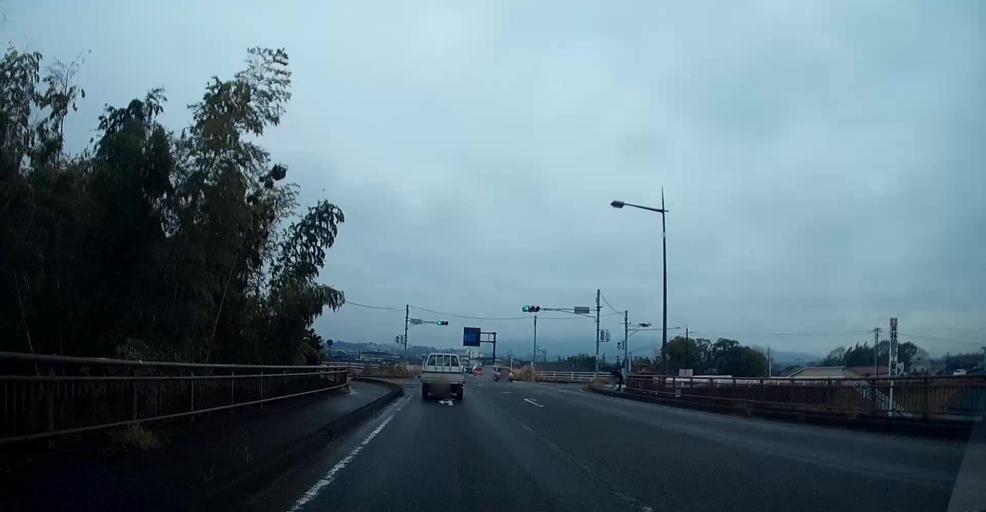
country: JP
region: Kumamoto
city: Kumamoto
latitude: 32.7338
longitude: 130.7390
